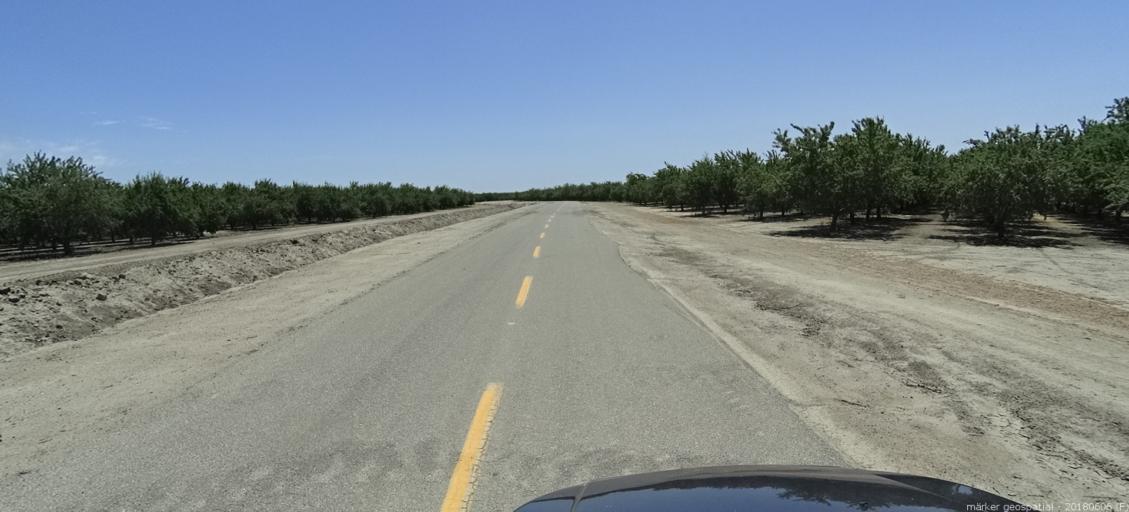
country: US
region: California
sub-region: Fresno County
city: Mendota
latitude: 36.8170
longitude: -120.3673
